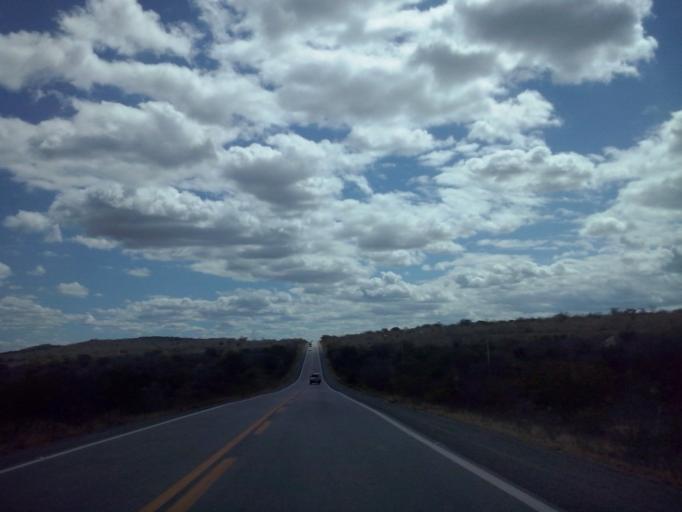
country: BR
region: Paraiba
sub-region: Soledade
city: Soledade
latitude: -7.0428
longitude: -36.3996
